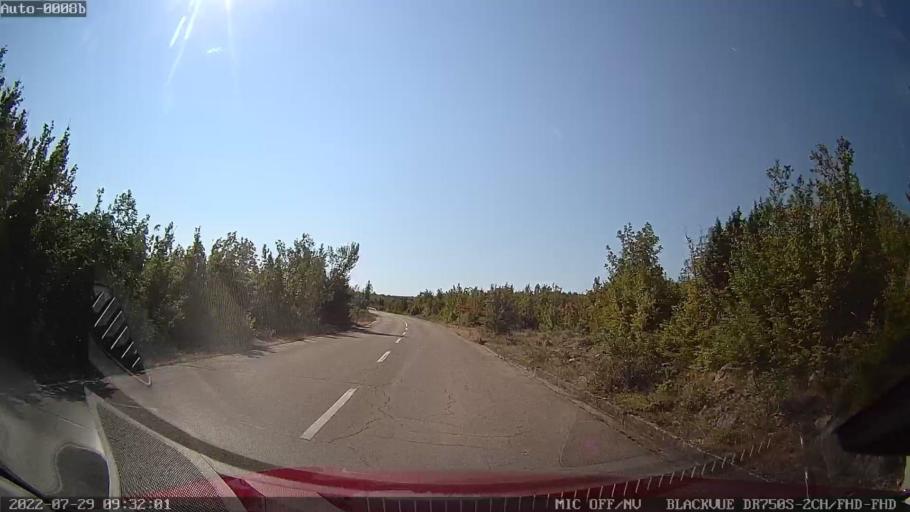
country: HR
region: Zadarska
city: Obrovac
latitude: 44.1845
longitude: 15.7060
